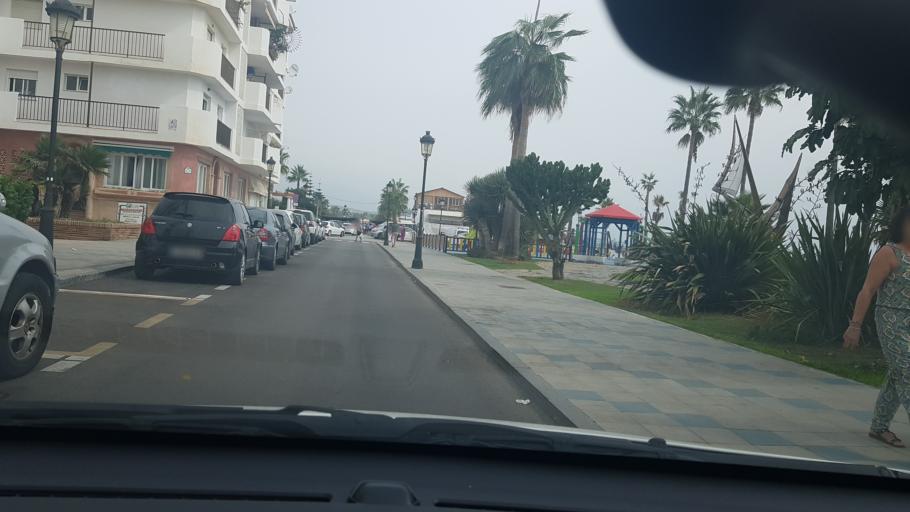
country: ES
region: Andalusia
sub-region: Provincia de Malaga
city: Manilva
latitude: 36.3692
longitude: -5.2245
